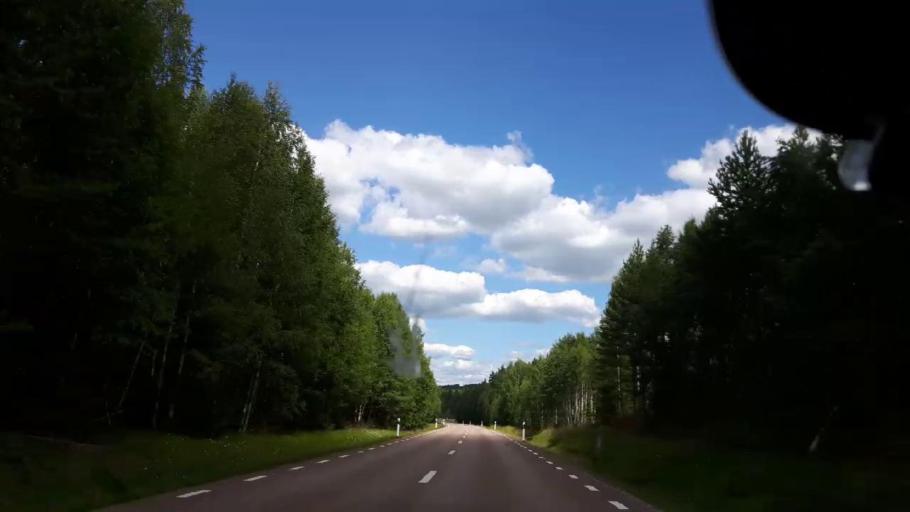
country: SE
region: Jaemtland
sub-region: Ragunda Kommun
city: Hammarstrand
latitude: 62.9023
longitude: 16.6997
